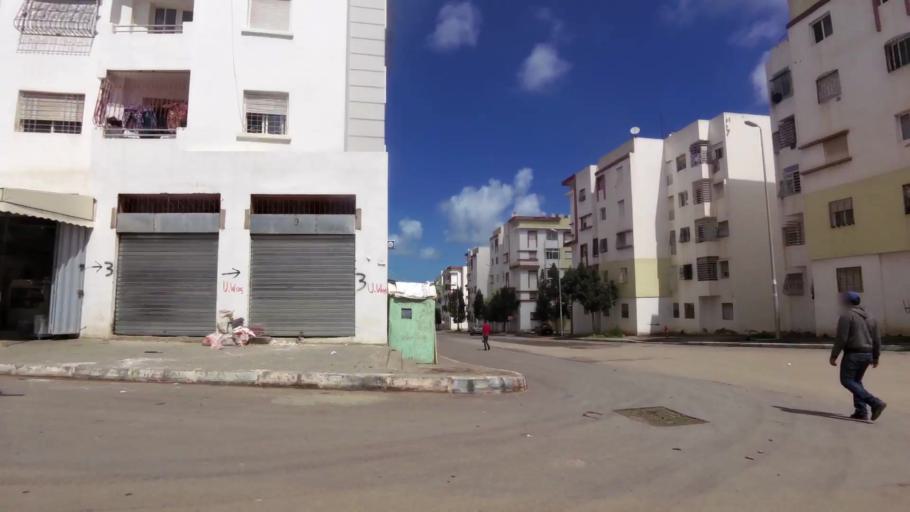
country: MA
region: Grand Casablanca
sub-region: Nouaceur
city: Dar Bouazza
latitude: 33.5333
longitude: -7.7172
